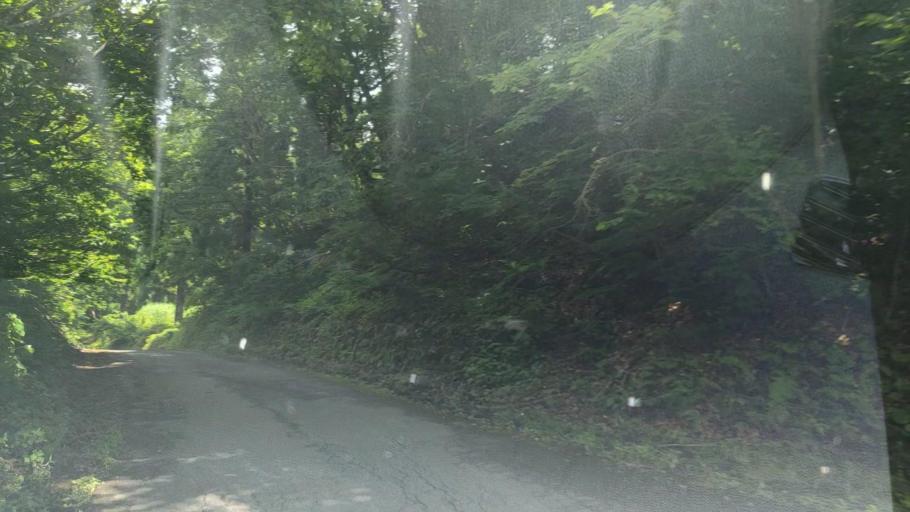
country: JP
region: Fukui
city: Ono
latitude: 35.8194
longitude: 136.4536
